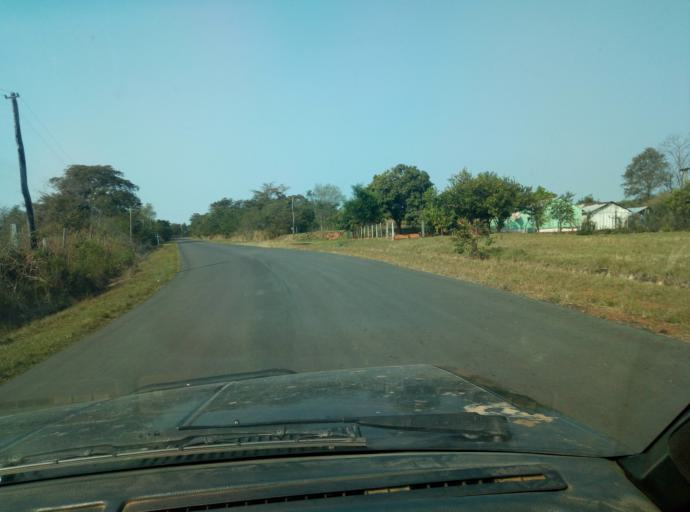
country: PY
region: Caaguazu
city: Carayao
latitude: -25.1874
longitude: -56.3125
